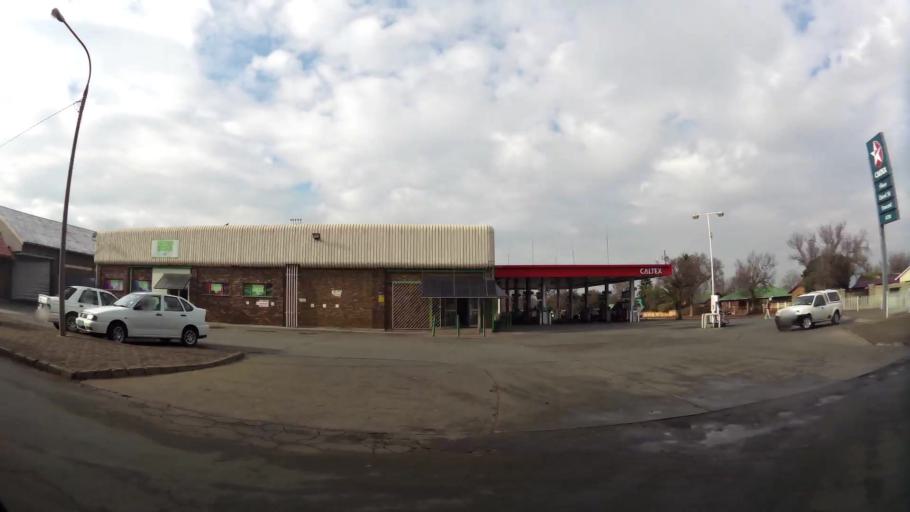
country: ZA
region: Gauteng
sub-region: Sedibeng District Municipality
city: Vanderbijlpark
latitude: -26.7022
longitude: 27.8149
